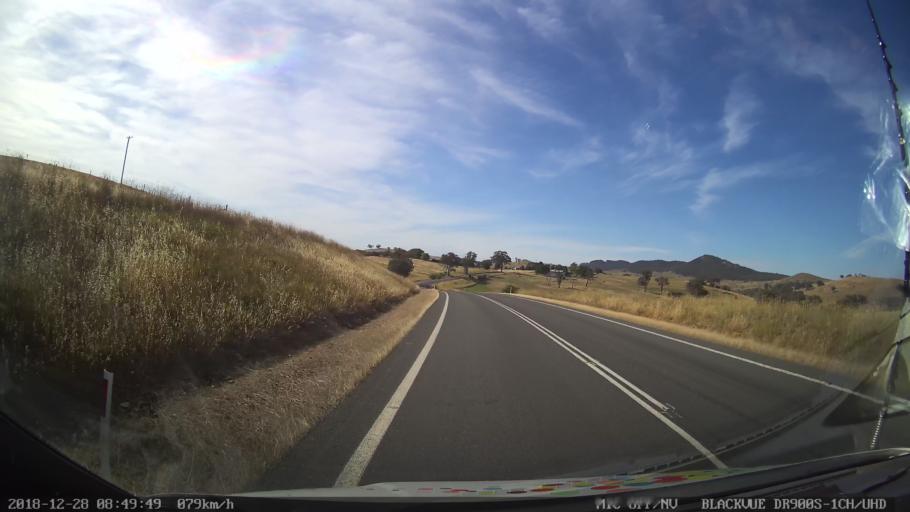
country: AU
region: New South Wales
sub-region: Upper Lachlan Shire
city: Crookwell
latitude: -34.0499
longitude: 149.3379
